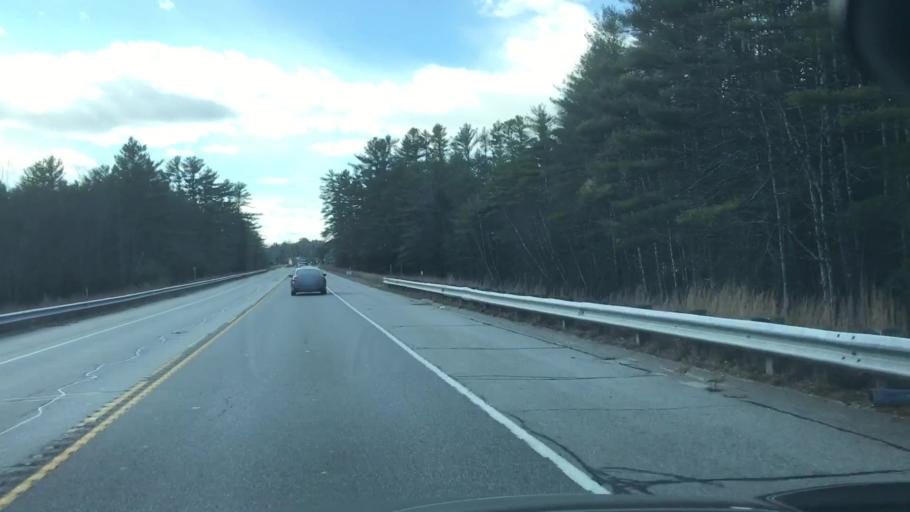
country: US
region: New Hampshire
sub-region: Merrimack County
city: Pittsfield
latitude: 43.3024
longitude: -71.3437
